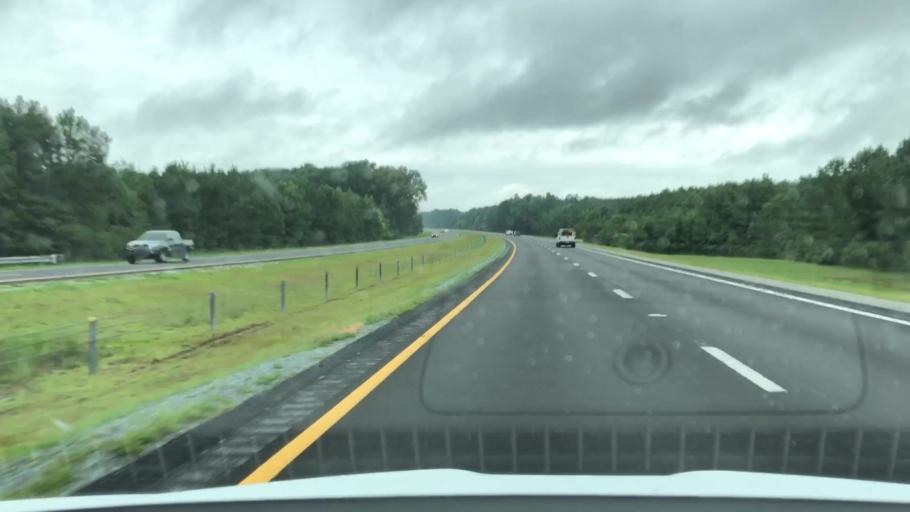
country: US
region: North Carolina
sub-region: Wayne County
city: Fremont
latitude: 35.4732
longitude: -77.9871
